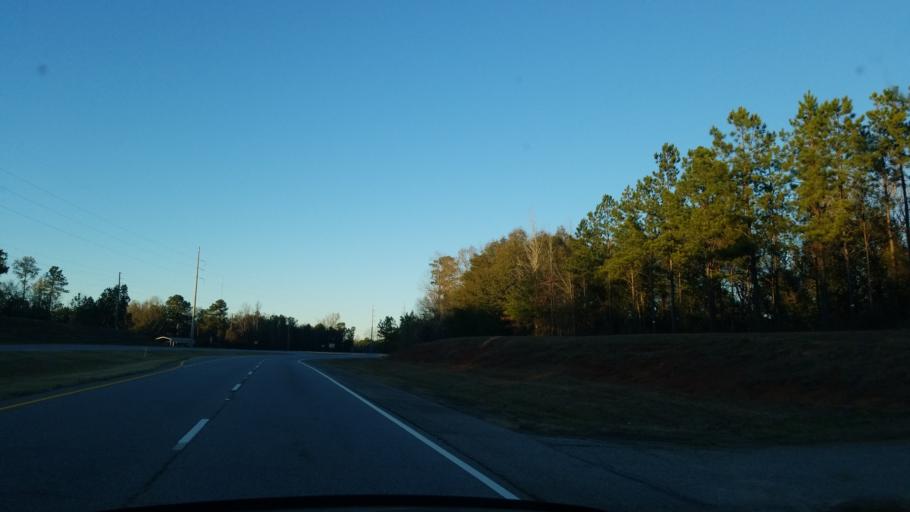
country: US
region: Georgia
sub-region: Chattahoochee County
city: Cusseta
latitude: 32.2783
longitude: -84.7811
